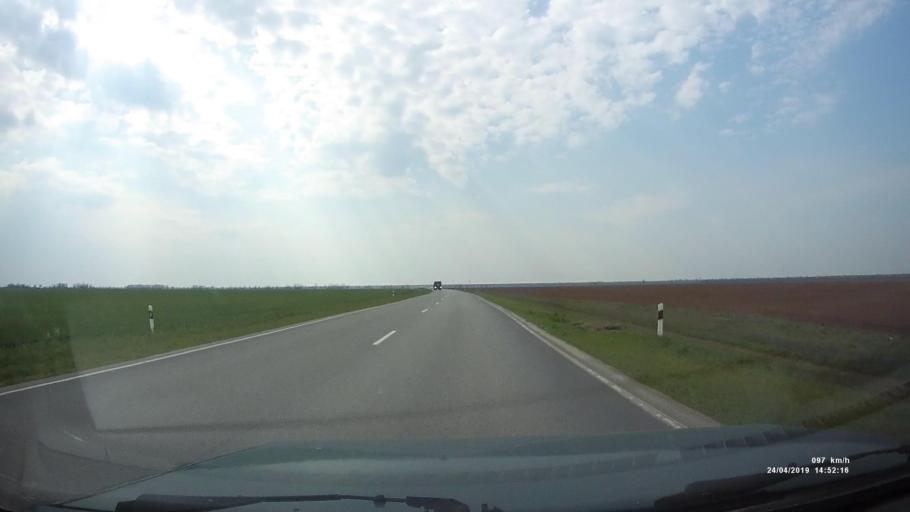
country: RU
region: Rostov
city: Remontnoye
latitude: 46.5299
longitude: 43.6843
